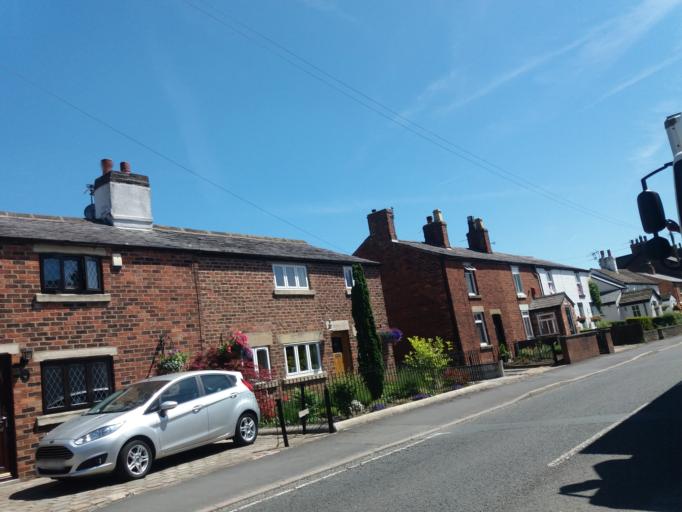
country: GB
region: England
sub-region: Lancashire
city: Croston
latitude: 53.6642
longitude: -2.7757
